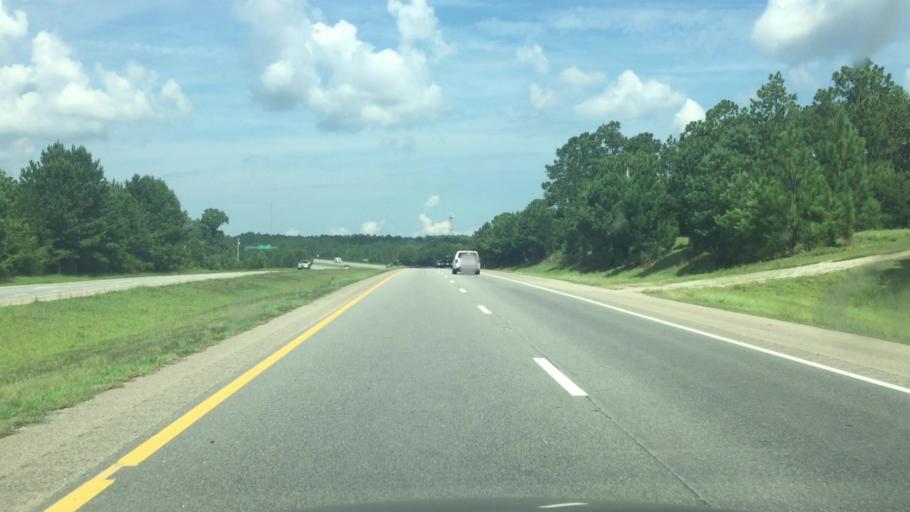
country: US
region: North Carolina
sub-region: Richmond County
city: Hamlet
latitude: 34.8654
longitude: -79.6389
